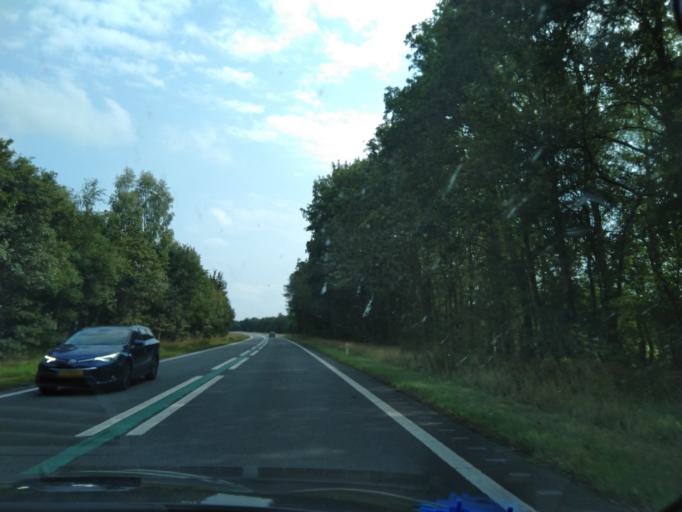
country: NL
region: Drenthe
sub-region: Gemeente Coevorden
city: Sleen
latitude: 52.8190
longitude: 6.6528
